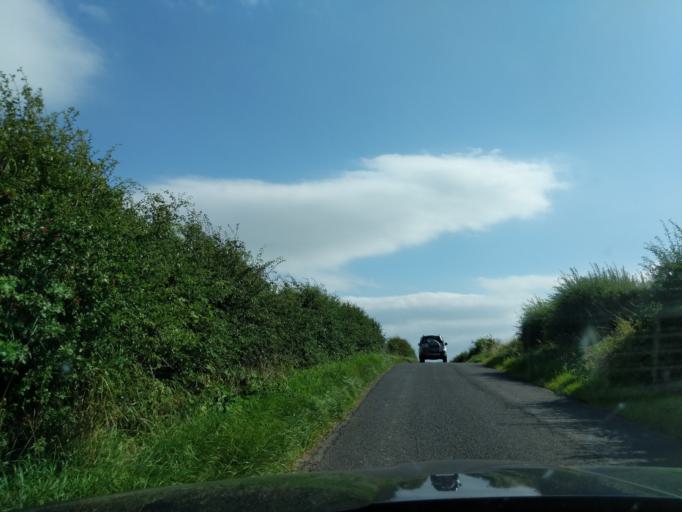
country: GB
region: England
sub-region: Northumberland
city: Ford
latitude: 55.6635
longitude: -2.1594
